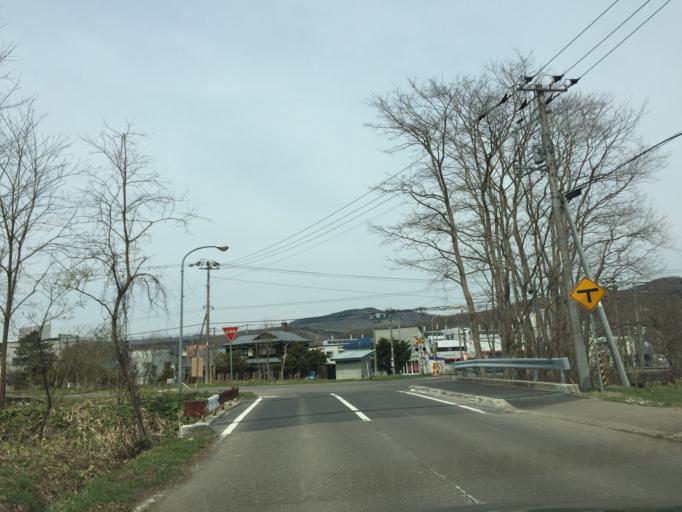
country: JP
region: Hokkaido
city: Akabira
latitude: 43.5512
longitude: 142.0549
